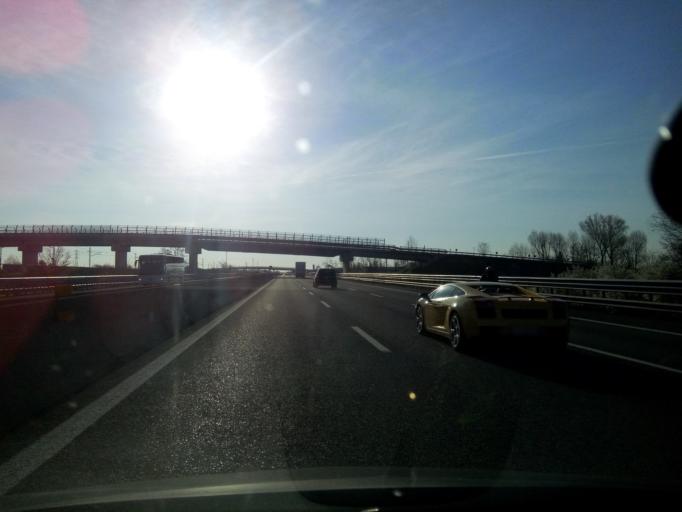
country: IT
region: Emilia-Romagna
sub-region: Provincia di Parma
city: Baganzola
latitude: 44.8558
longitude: 10.2725
